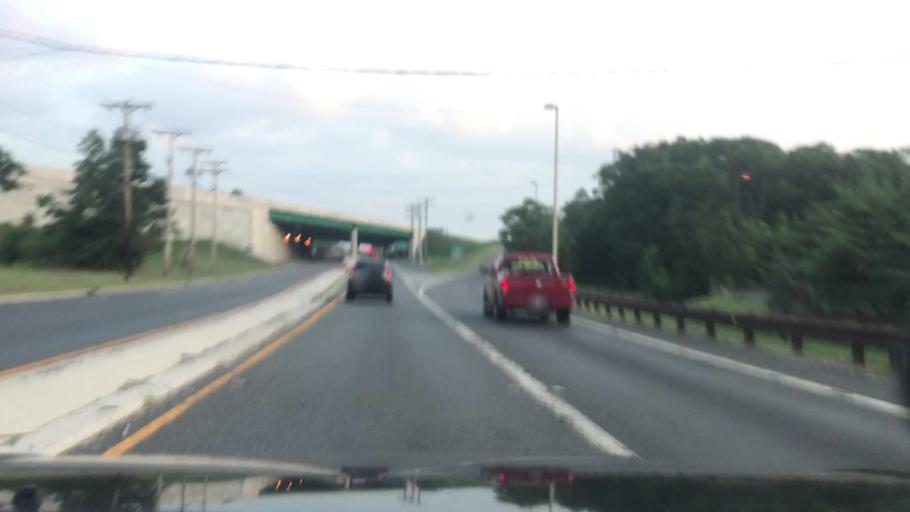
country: US
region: New Jersey
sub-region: Ocean County
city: Silver Ridge
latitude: 39.9905
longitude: -74.2111
